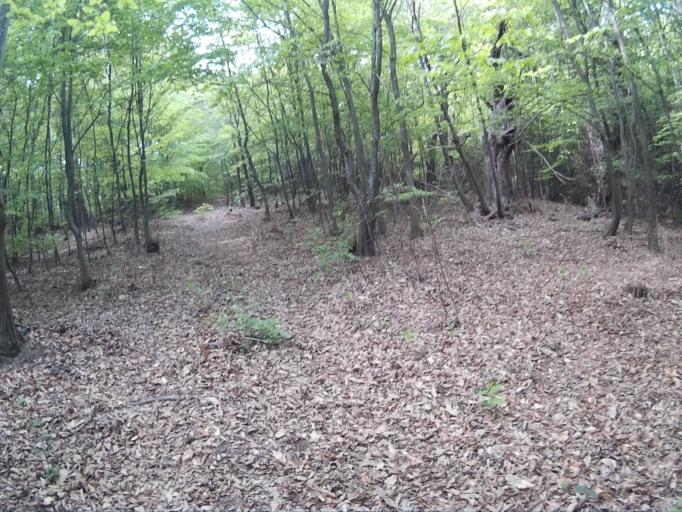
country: HU
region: Vas
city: Koszeg
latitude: 47.3639
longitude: 16.5043
